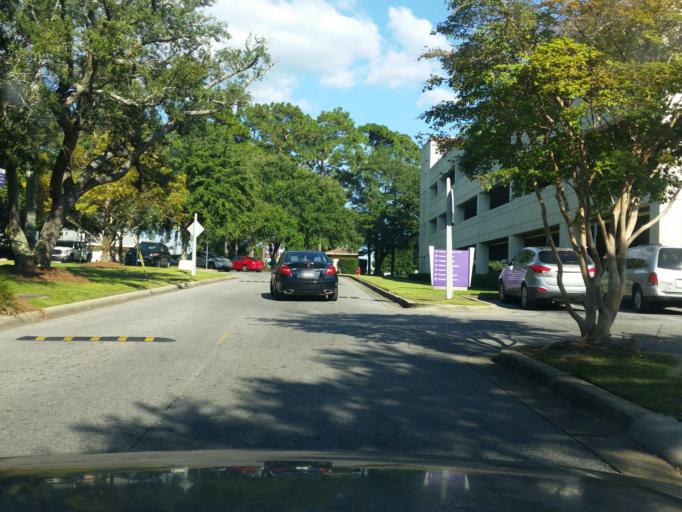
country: US
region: Florida
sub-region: Escambia County
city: Brent
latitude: 30.4784
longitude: -87.2121
